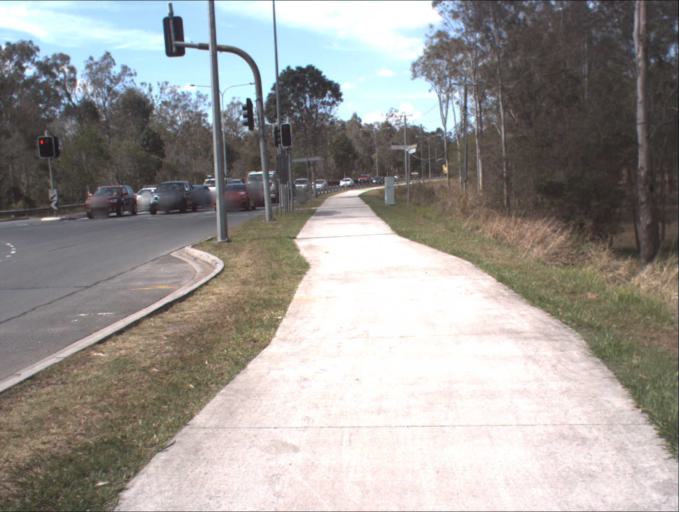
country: AU
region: Queensland
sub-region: Logan
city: Slacks Creek
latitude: -27.6577
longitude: 153.1427
